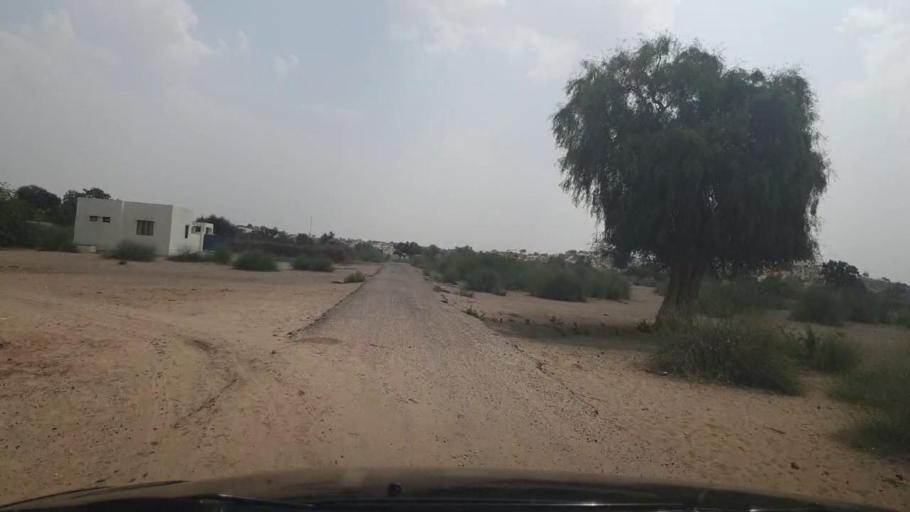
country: PK
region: Sindh
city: Islamkot
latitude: 24.9918
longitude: 70.4965
